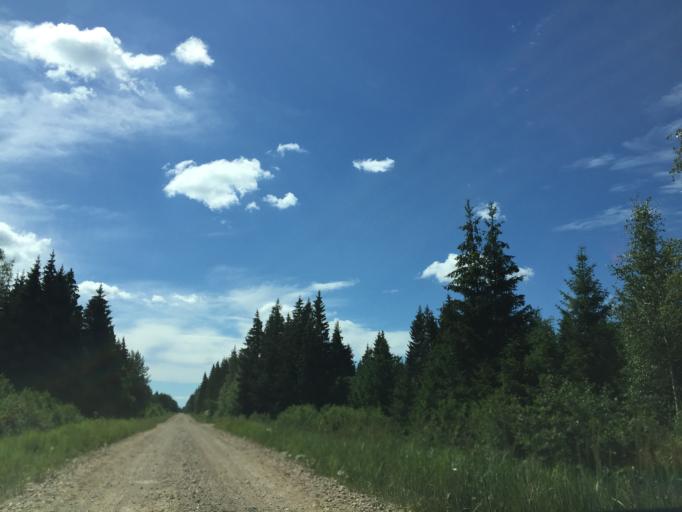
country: LV
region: Ventspils Rajons
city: Piltene
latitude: 57.2735
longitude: 21.8333
